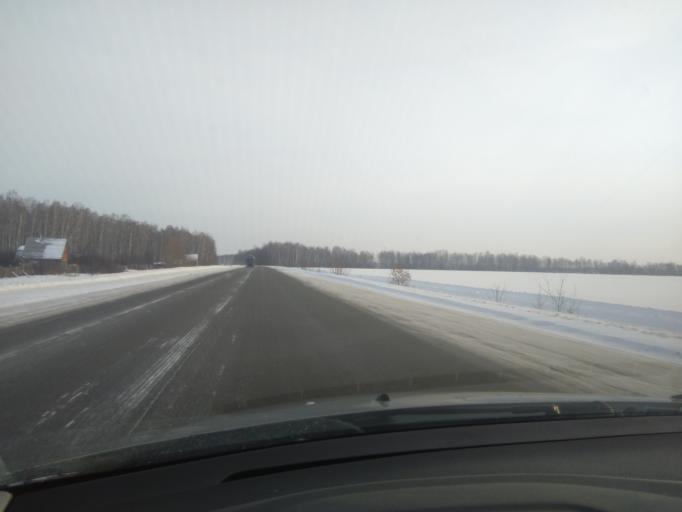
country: RU
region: Sverdlovsk
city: Bogdanovich
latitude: 56.7998
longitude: 62.0146
